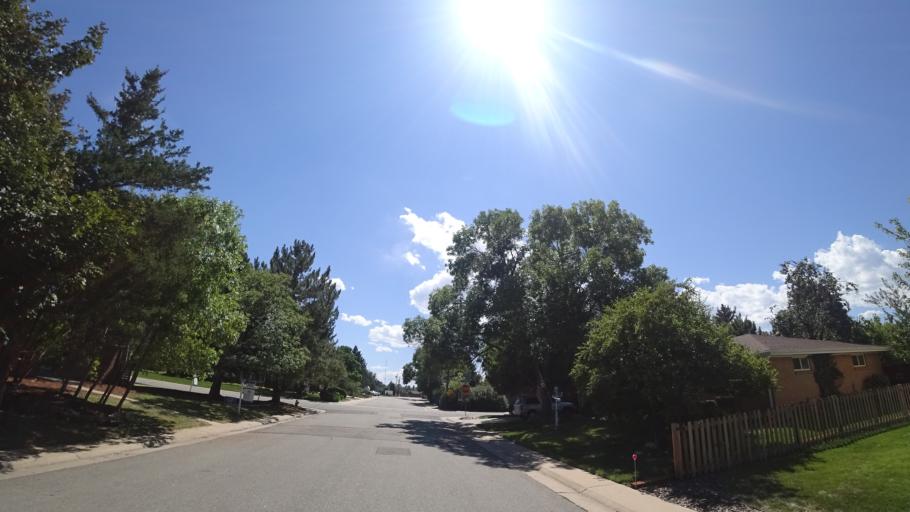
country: US
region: Colorado
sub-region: Arapahoe County
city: Greenwood Village
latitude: 39.6082
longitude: -104.9799
